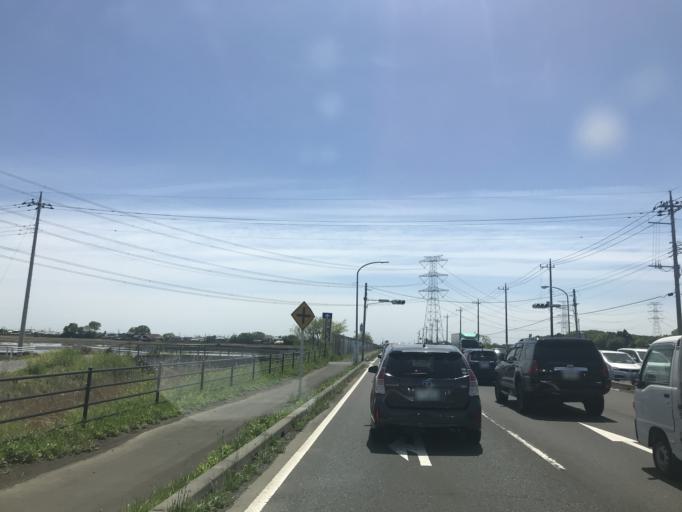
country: JP
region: Ibaraki
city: Shimodate
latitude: 36.2465
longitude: 139.9836
